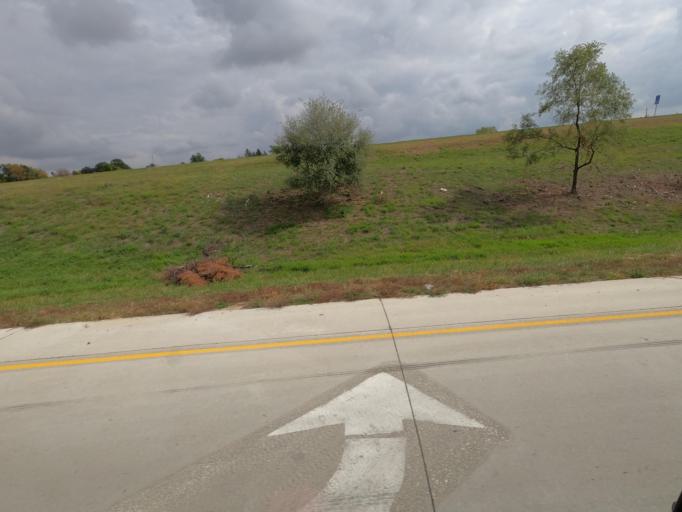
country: US
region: Iowa
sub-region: Polk County
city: Pleasant Hill
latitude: 41.6003
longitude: -93.4982
